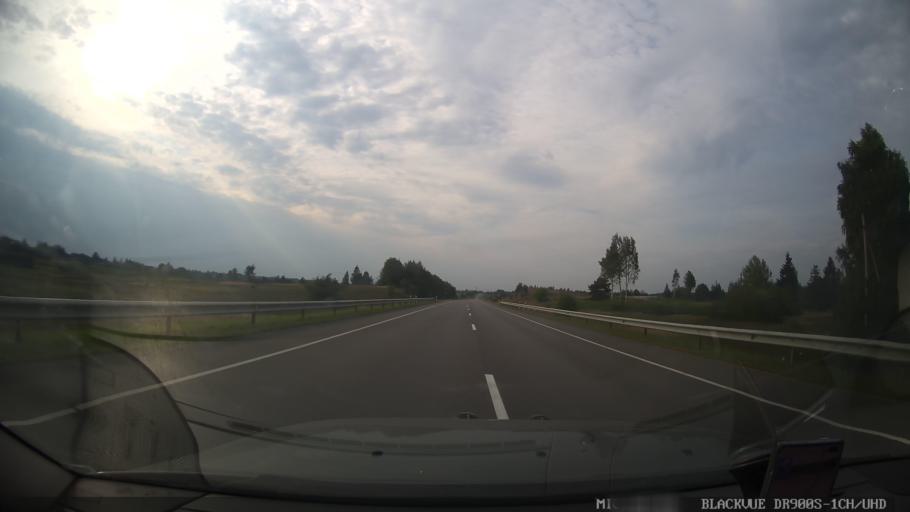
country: LT
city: Skaidiskes
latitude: 54.6166
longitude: 25.4227
